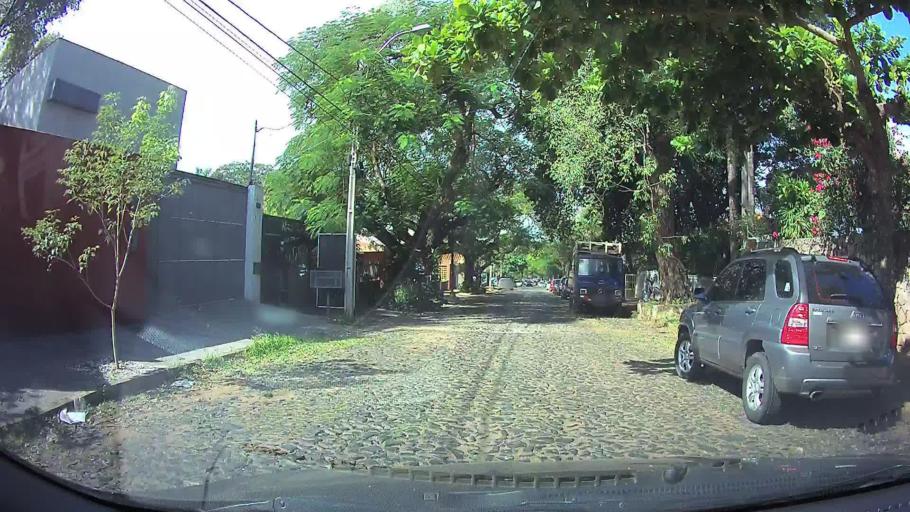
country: PY
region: Asuncion
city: Asuncion
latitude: -25.2985
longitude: -57.6008
